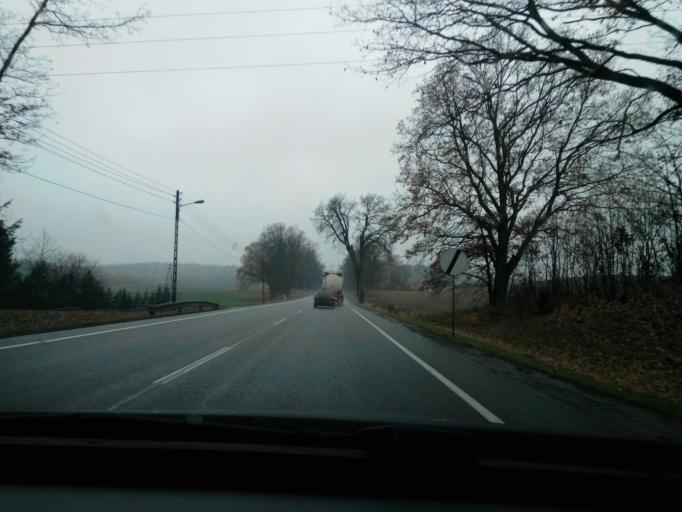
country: PL
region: Pomeranian Voivodeship
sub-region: Powiat tczewski
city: Subkowy
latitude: 54.0456
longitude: 18.7268
